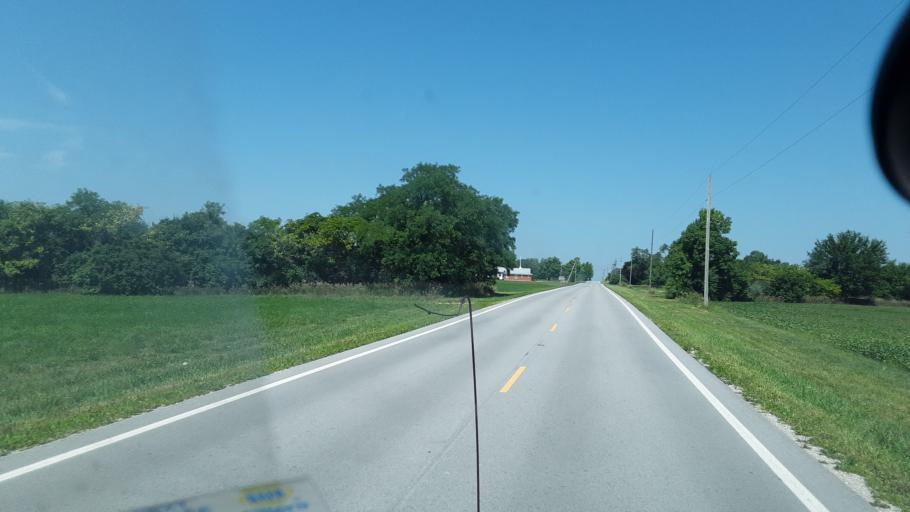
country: US
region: Ohio
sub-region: Wyandot County
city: Carey
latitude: 40.9831
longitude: -83.4475
